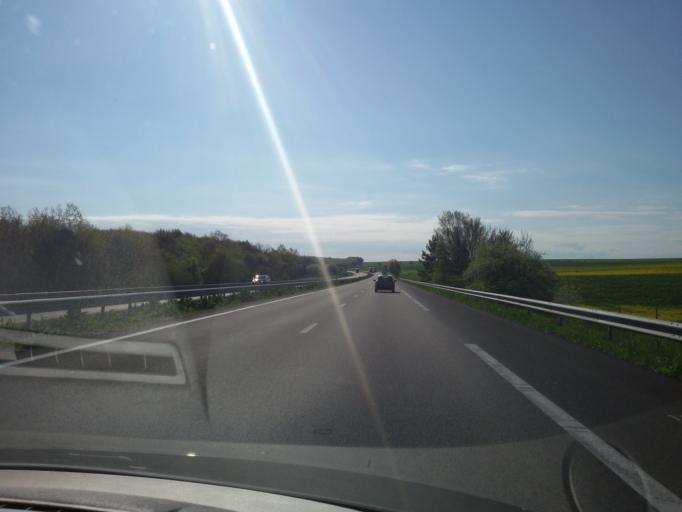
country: FR
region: Bourgogne
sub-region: Departement de l'Yonne
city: Vermenton
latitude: 47.7035
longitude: 3.8025
